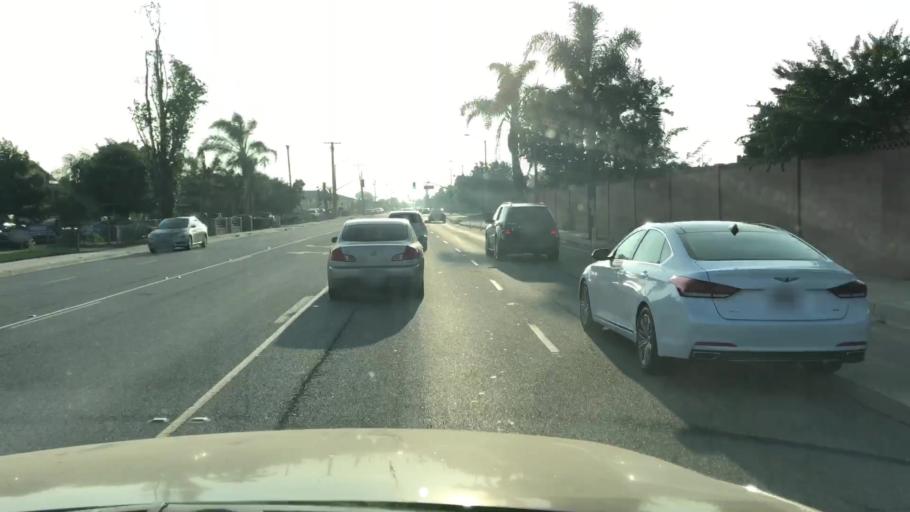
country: US
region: California
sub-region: Ventura County
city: Port Hueneme
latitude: 34.1548
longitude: -119.1713
